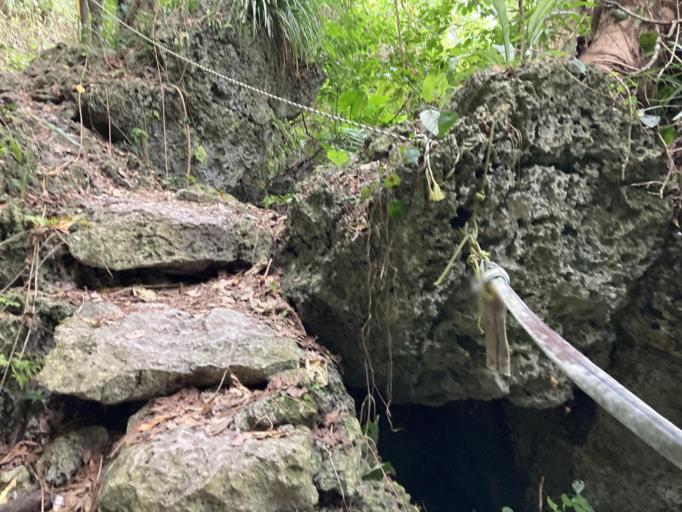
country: JP
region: Okinawa
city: Tomigusuku
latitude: 26.1437
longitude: 127.7807
